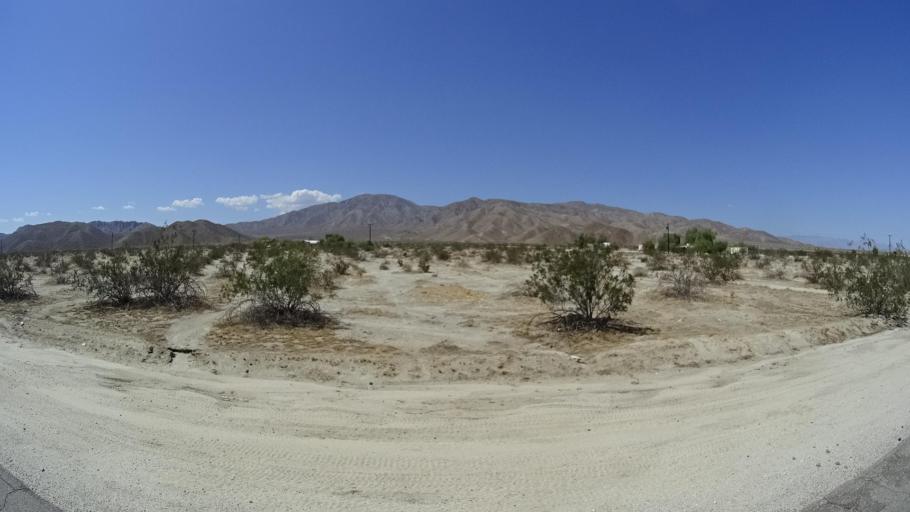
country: US
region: California
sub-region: Imperial County
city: Salton City
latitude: 33.0771
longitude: -116.1056
